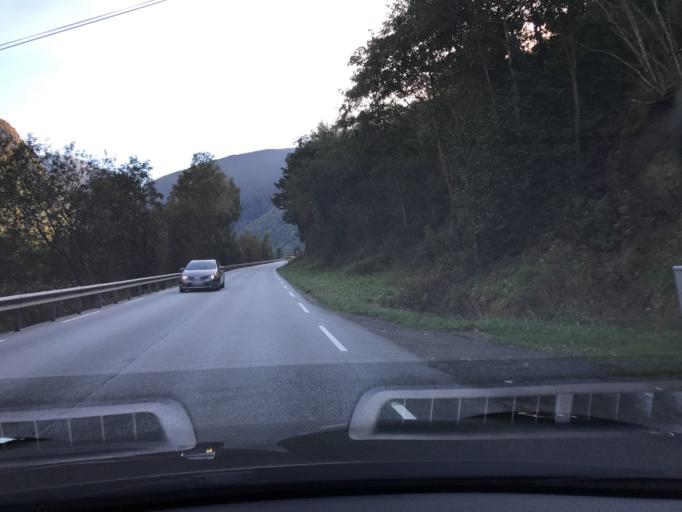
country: NO
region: Sogn og Fjordane
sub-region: Laerdal
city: Laerdalsoyri
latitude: 61.0923
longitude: 7.5168
